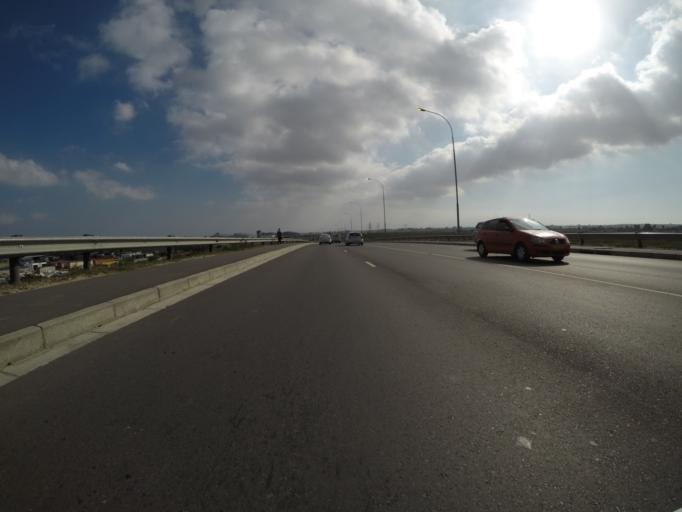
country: ZA
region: Western Cape
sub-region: City of Cape Town
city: Kraaifontein
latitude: -33.9533
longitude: 18.6925
